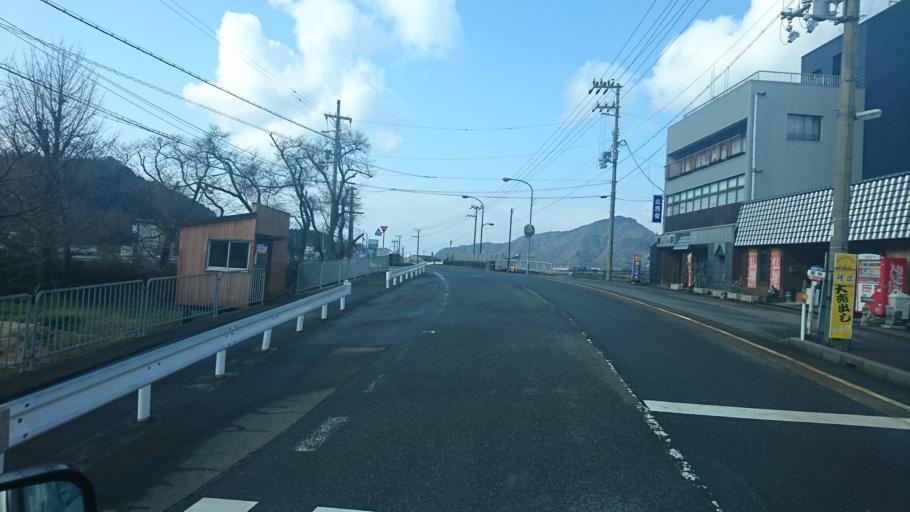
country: JP
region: Tottori
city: Tottori
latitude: 35.6090
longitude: 134.4719
